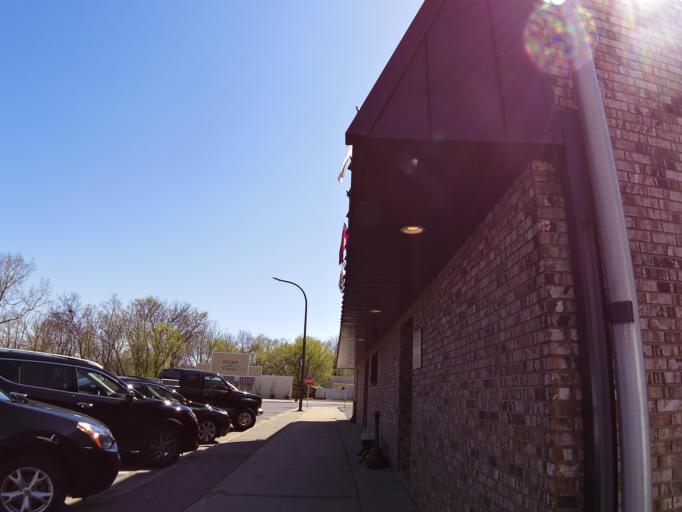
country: US
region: Minnesota
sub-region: Scott County
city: Prior Lake
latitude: 44.7131
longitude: -93.4248
